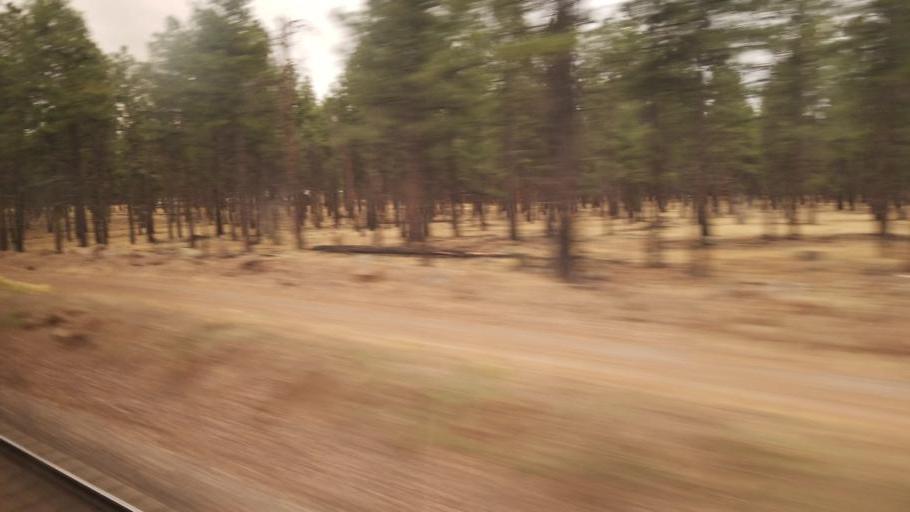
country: US
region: Arizona
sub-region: Coconino County
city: Parks
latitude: 35.2454
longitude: -112.0471
